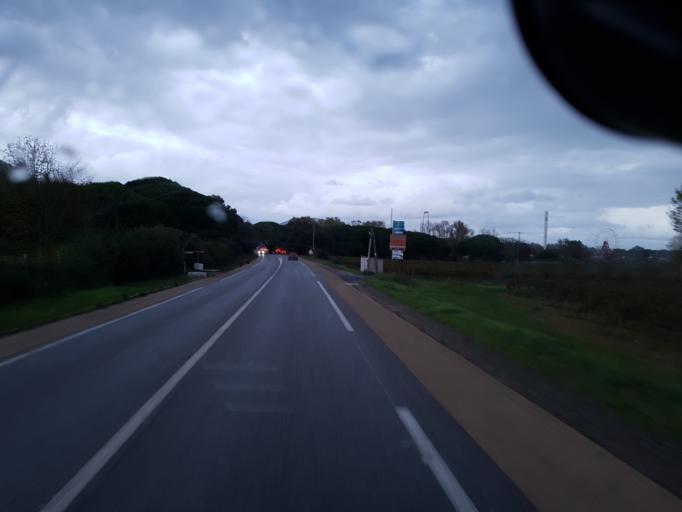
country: FR
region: Provence-Alpes-Cote d'Azur
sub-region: Departement du Var
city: Gassin
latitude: 43.2568
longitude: 6.5749
